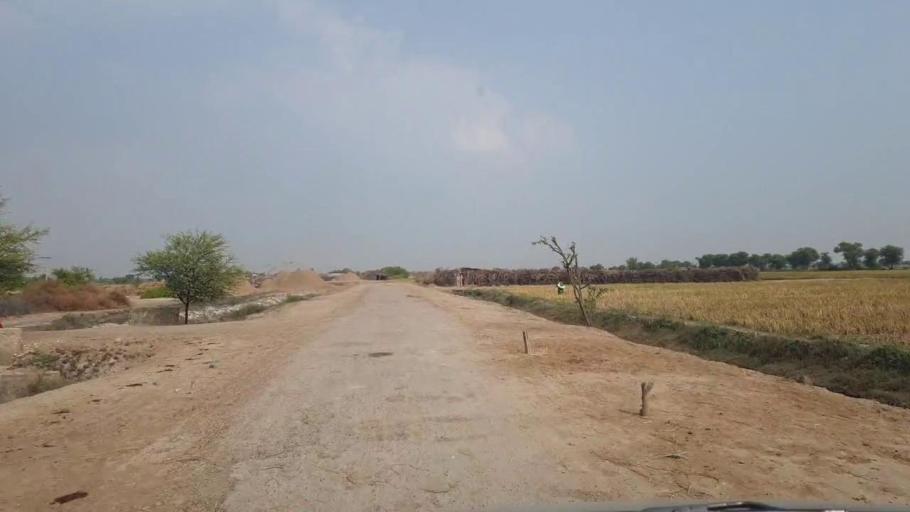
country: PK
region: Sindh
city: Matli
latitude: 24.9619
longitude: 68.6880
